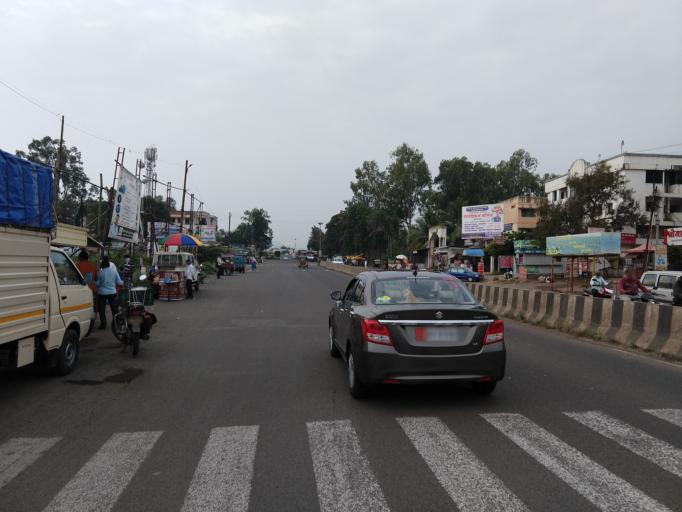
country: IN
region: Maharashtra
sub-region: Pune Division
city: Sasvad
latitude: 18.3504
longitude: 74.0288
